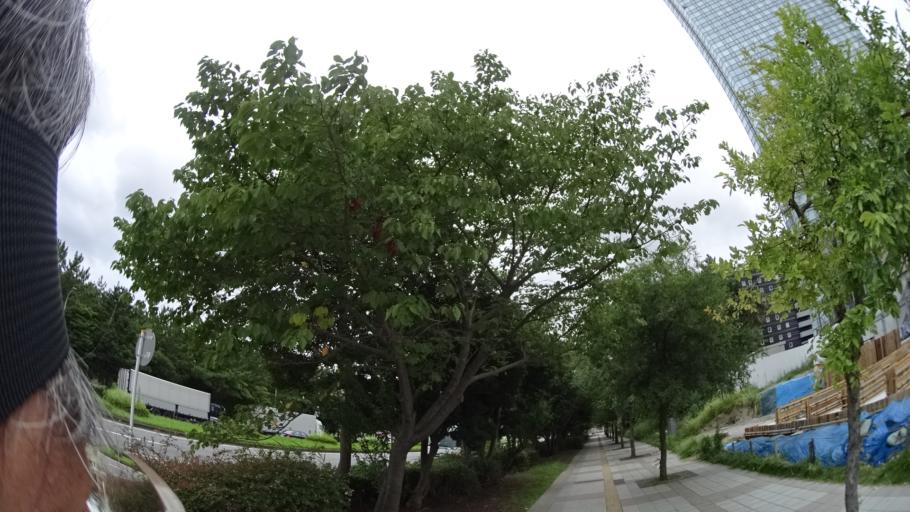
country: JP
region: Chiba
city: Funabashi
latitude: 35.6432
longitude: 140.0371
